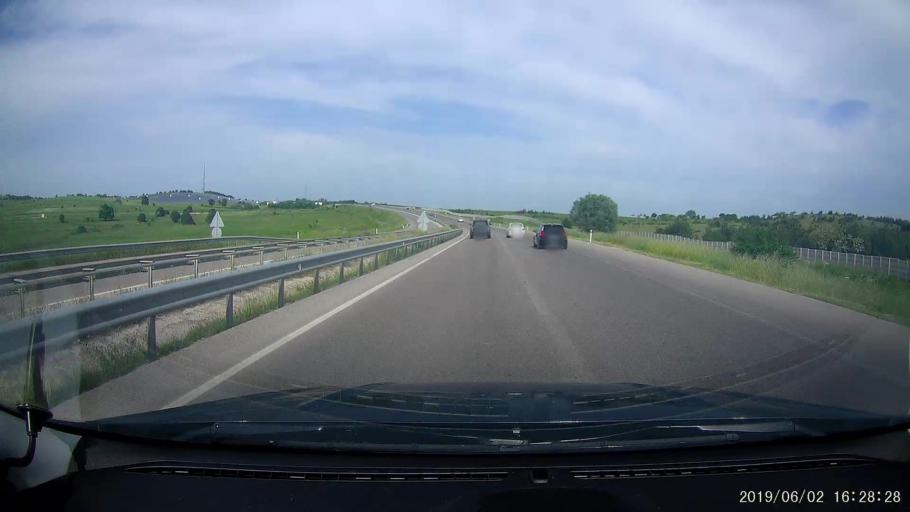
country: TR
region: Samsun
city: Ladik
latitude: 41.0069
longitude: 35.8482
